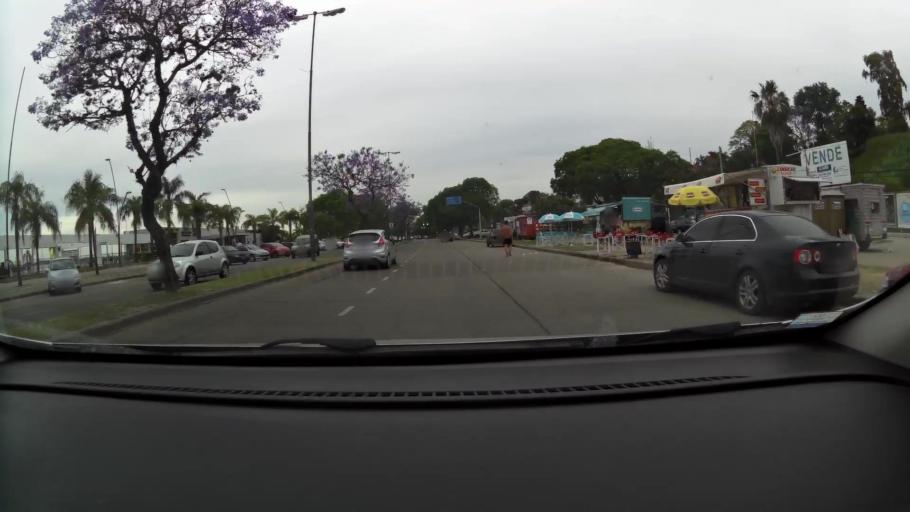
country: AR
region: Santa Fe
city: Granadero Baigorria
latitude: -32.8877
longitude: -60.6873
